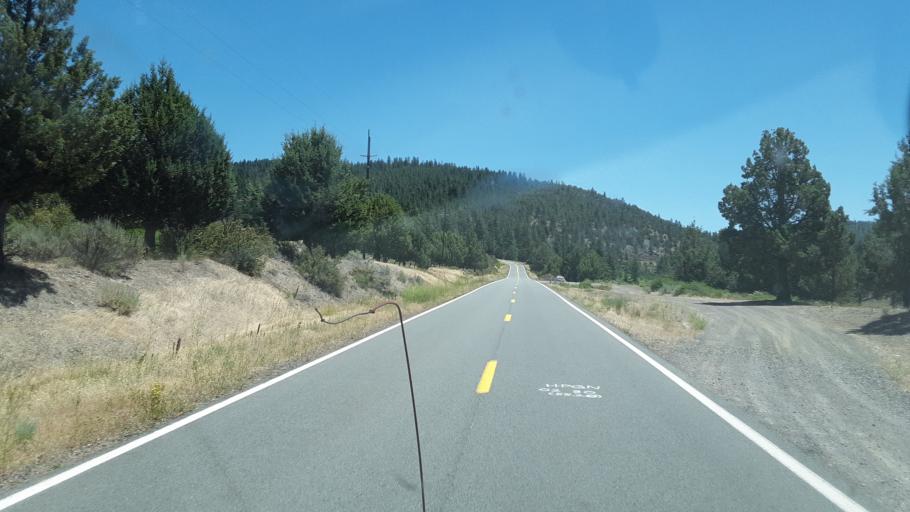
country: US
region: California
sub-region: Modoc County
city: Alturas
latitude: 41.0382
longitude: -120.8597
